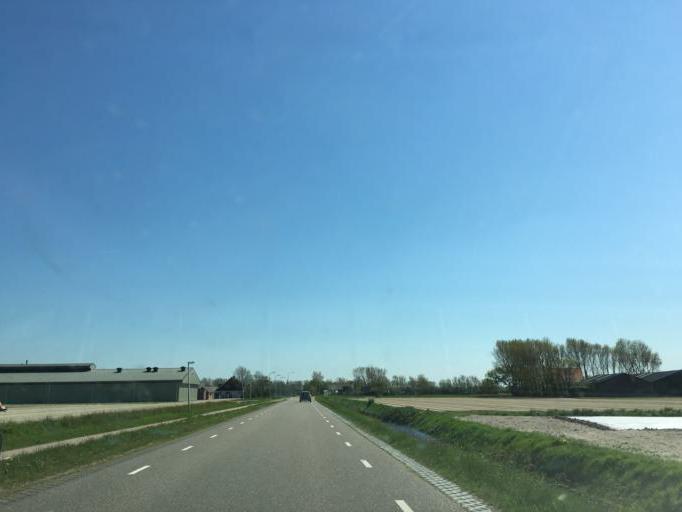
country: NL
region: North Holland
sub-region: Gemeente Schagen
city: Schagen
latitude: 52.8439
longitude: 4.7435
